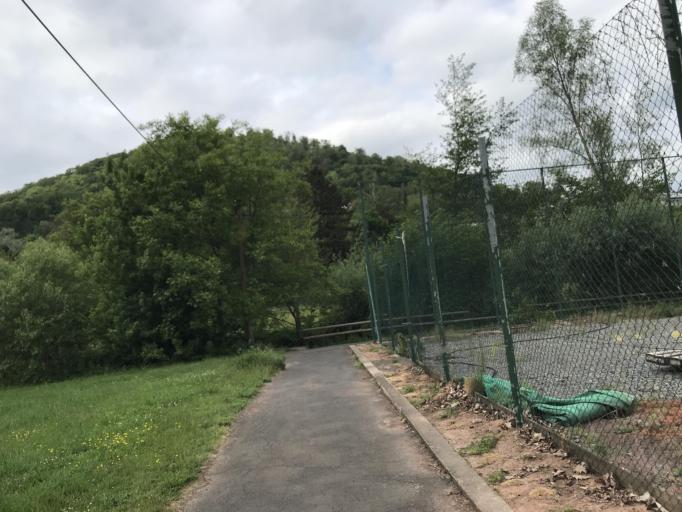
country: DE
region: Hesse
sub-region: Regierungsbezirk Kassel
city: Zierenberg
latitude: 51.3709
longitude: 9.3044
